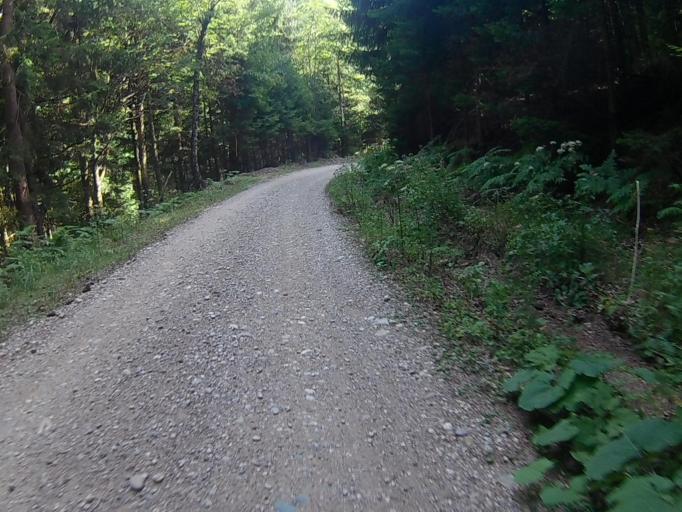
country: SI
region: Ruse
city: Ruse
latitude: 46.5151
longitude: 15.5434
